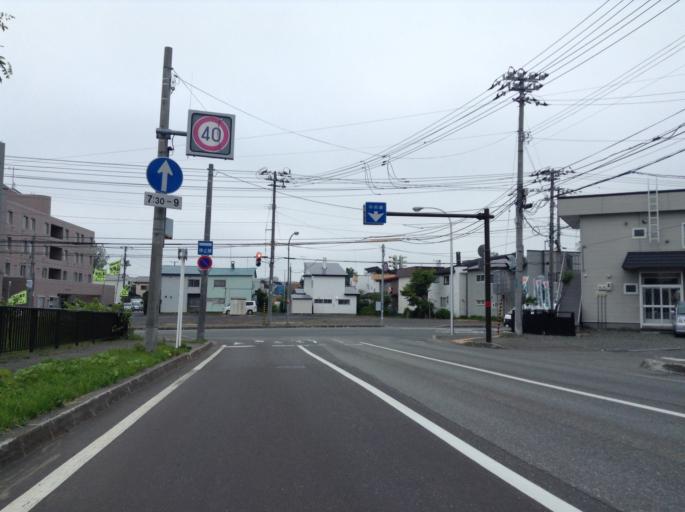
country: JP
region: Hokkaido
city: Wakkanai
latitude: 45.3959
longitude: 141.6859
